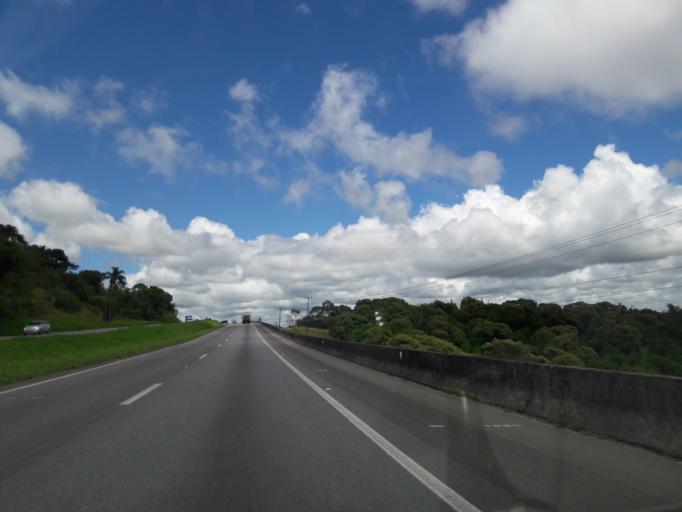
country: BR
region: Parana
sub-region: Campina Grande Do Sul
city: Campina Grande do Sul
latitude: -25.1455
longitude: -48.8582
